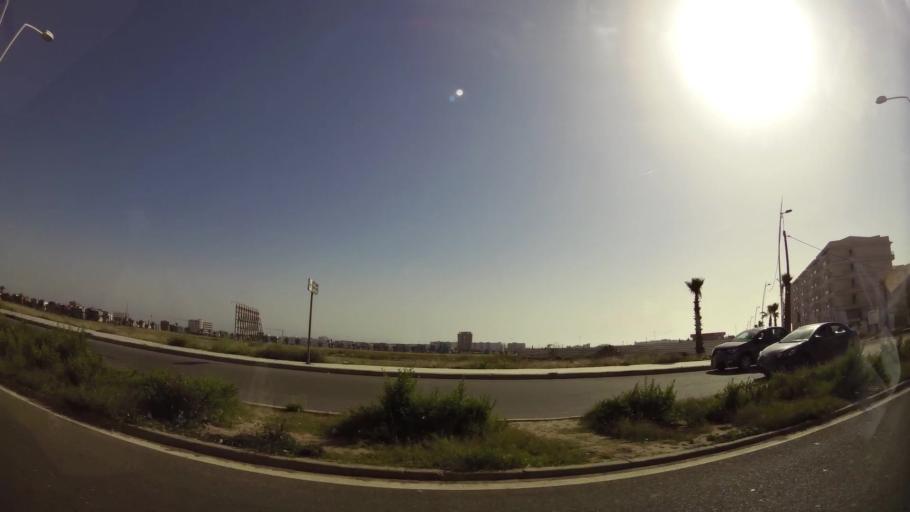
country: MA
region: Oued ed Dahab-Lagouira
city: Dakhla
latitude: 30.4069
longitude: -9.5642
